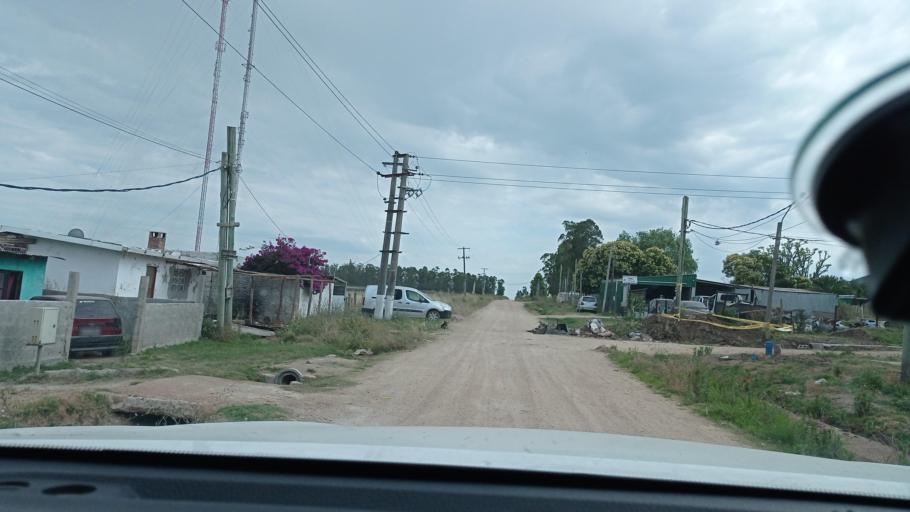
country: UY
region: Canelones
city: Pando
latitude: -34.7067
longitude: -55.9694
